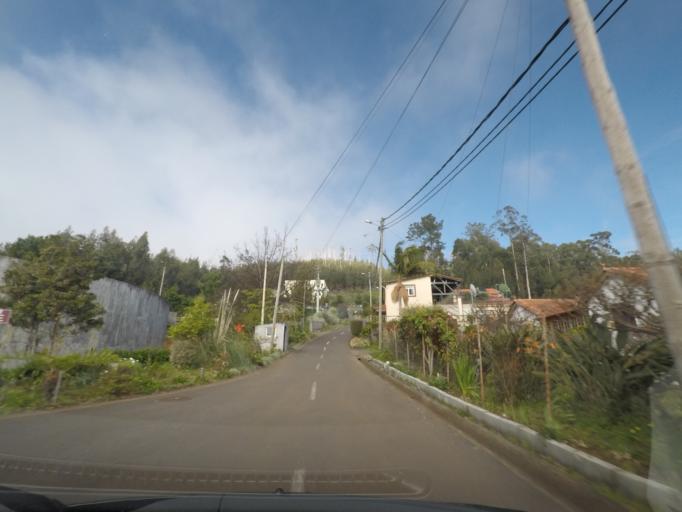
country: PT
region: Madeira
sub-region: Calheta
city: Estreito da Calheta
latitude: 32.7495
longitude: -17.1879
